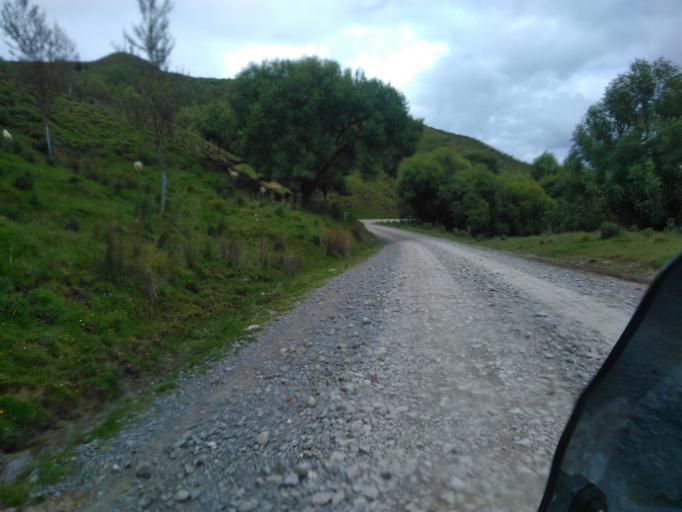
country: NZ
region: Gisborne
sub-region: Gisborne District
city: Gisborne
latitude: -38.0953
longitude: 178.1010
